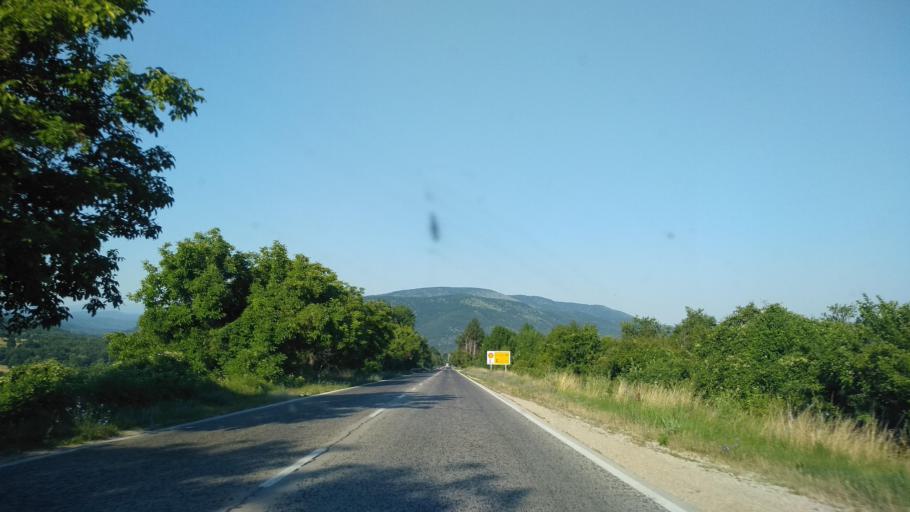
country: BG
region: Lovech
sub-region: Obshtina Lovech
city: Lovech
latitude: 43.0451
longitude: 24.7494
